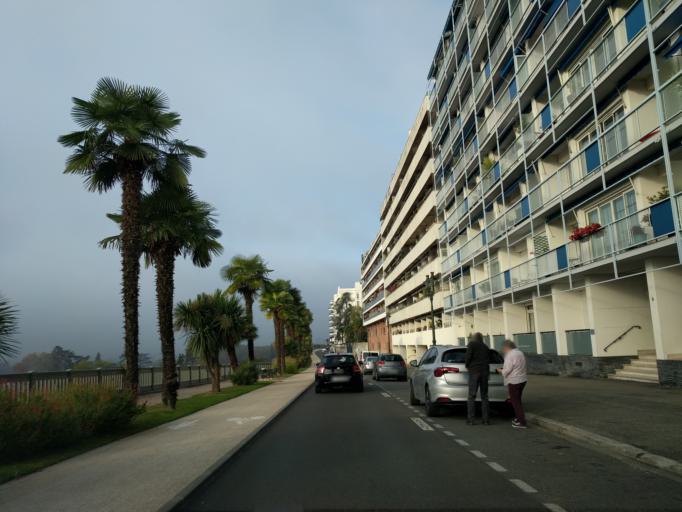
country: FR
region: Aquitaine
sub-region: Departement des Pyrenees-Atlantiques
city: Pau
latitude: 43.2939
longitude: -0.3642
